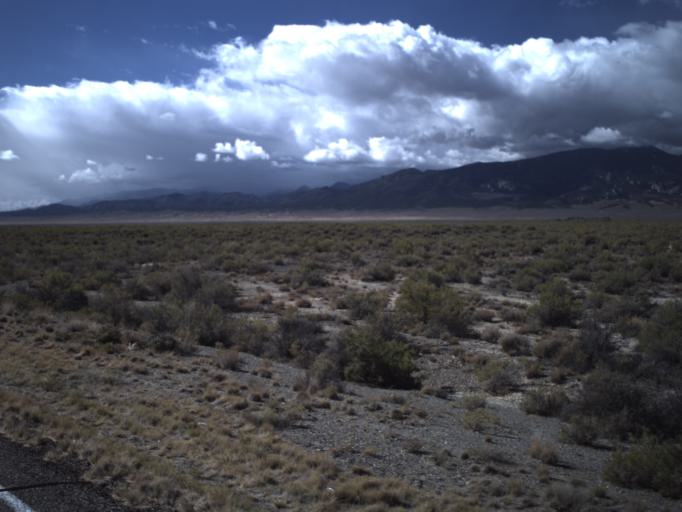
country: US
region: Nevada
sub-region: White Pine County
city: McGill
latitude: 39.0513
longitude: -114.0365
